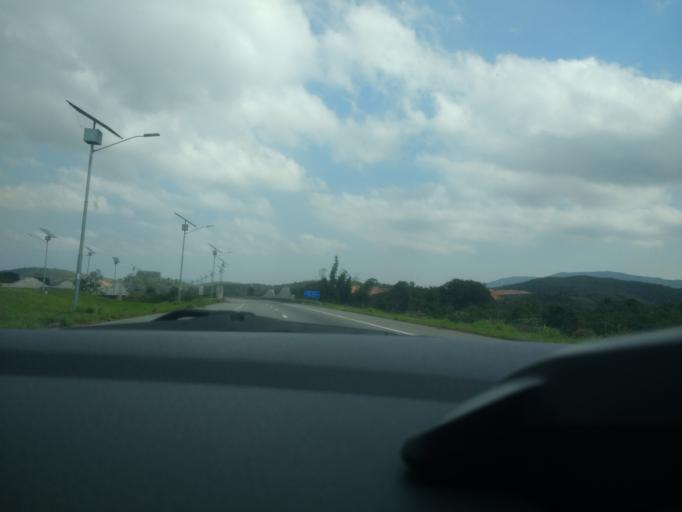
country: BR
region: Rio de Janeiro
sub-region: Queimados
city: Queimados
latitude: -22.6626
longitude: -43.5773
